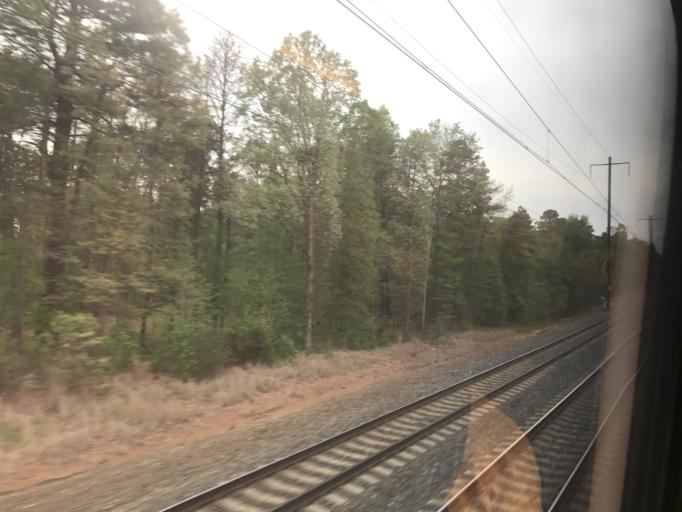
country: US
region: Maryland
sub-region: Anne Arundel County
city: Odenton
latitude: 39.0946
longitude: -76.7031
